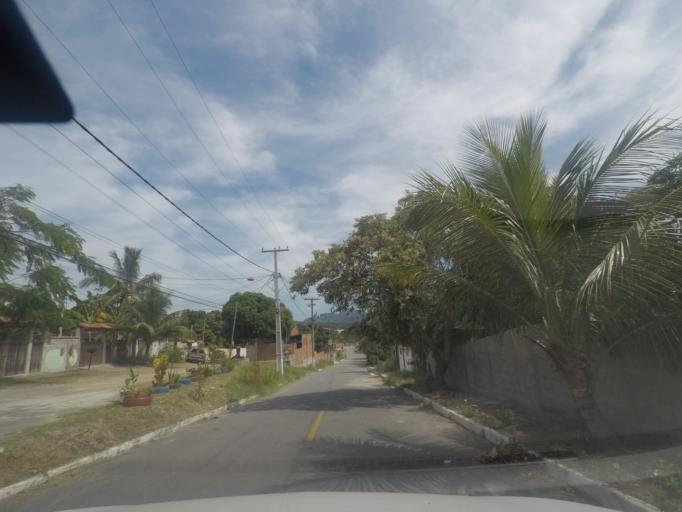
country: BR
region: Rio de Janeiro
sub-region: Marica
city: Marica
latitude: -22.9526
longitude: -42.7499
